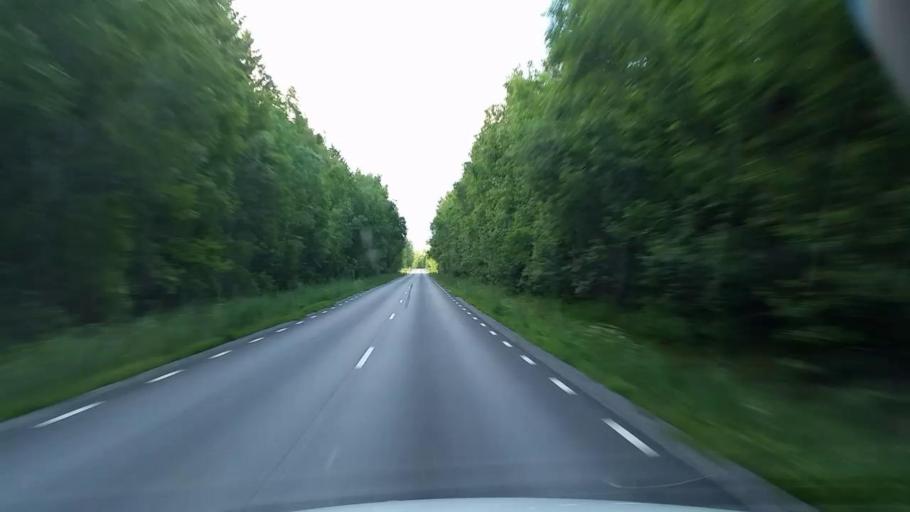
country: SE
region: Vaestmanland
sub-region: Kopings Kommun
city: Kolsva
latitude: 59.6716
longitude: 15.8385
